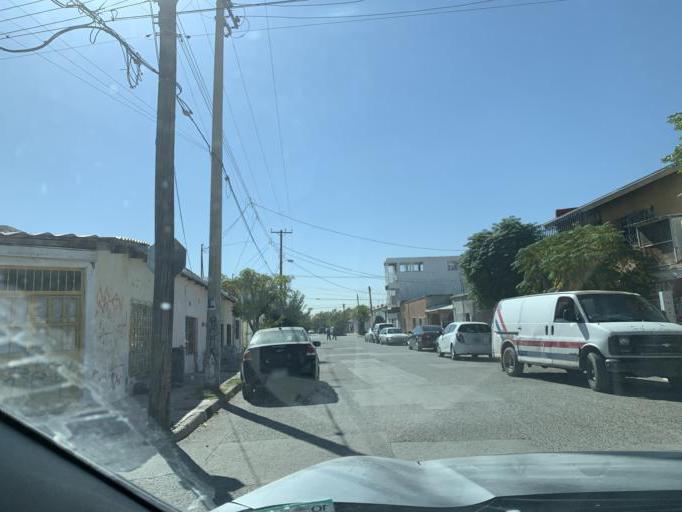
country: MX
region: Chihuahua
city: Ciudad Juarez
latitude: 31.7252
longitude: -106.4605
